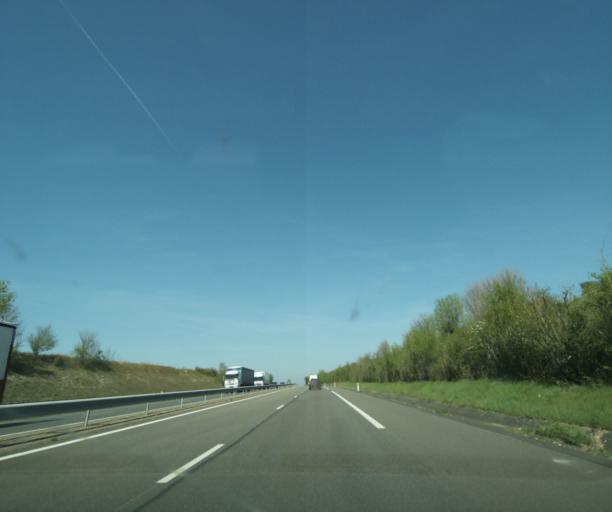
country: FR
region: Bourgogne
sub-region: Departement de la Nievre
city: La Charite-sur-Loire
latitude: 47.1700
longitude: 3.0489
